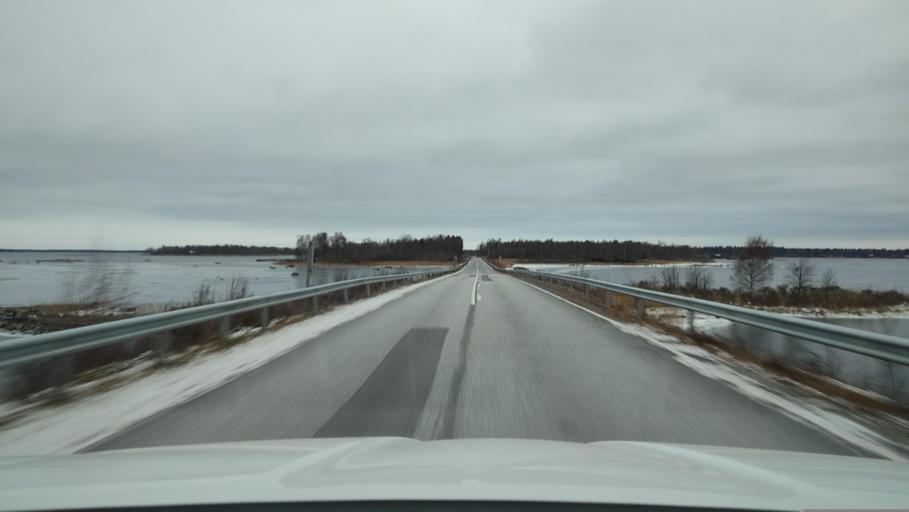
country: FI
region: Ostrobothnia
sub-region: Vaasa
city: Replot
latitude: 63.2745
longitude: 21.3437
